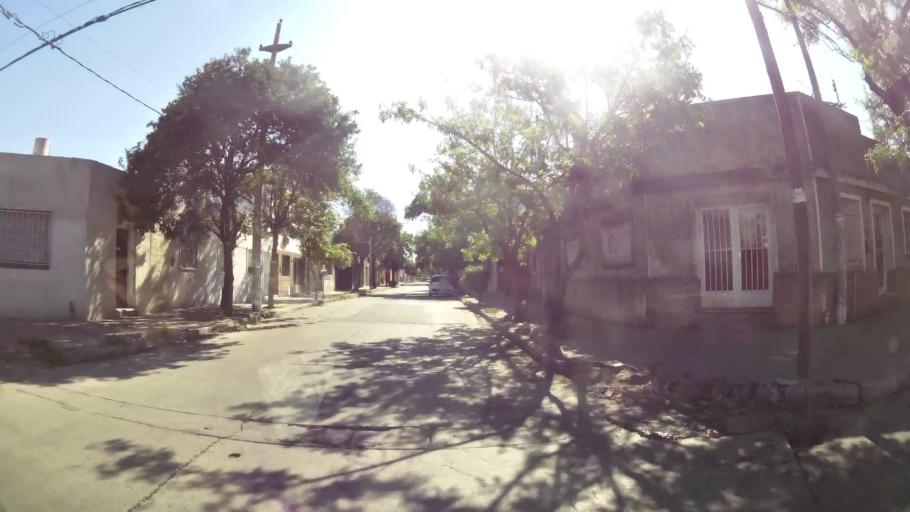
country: AR
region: Cordoba
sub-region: Departamento de Capital
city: Cordoba
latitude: -31.4050
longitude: -64.1553
